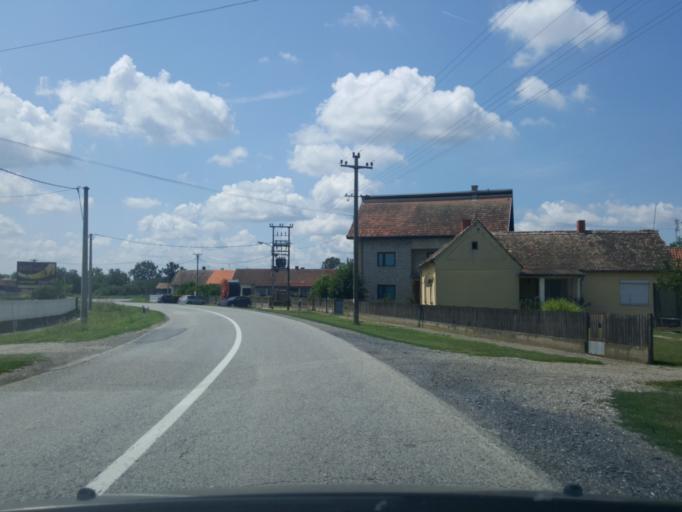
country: RS
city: Metkovic
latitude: 44.8524
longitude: 19.5352
